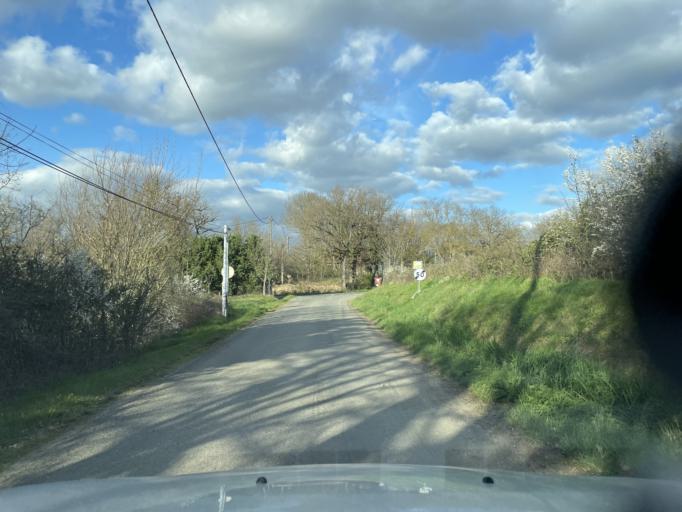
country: FR
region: Midi-Pyrenees
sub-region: Departement du Gers
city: Pujaudran
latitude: 43.6202
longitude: 1.1752
